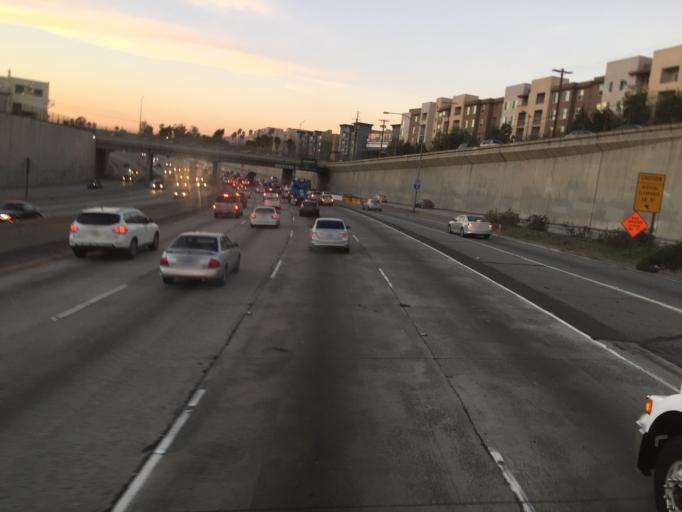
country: US
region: California
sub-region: Los Angeles County
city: Los Angeles
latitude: 34.0773
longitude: -118.2193
